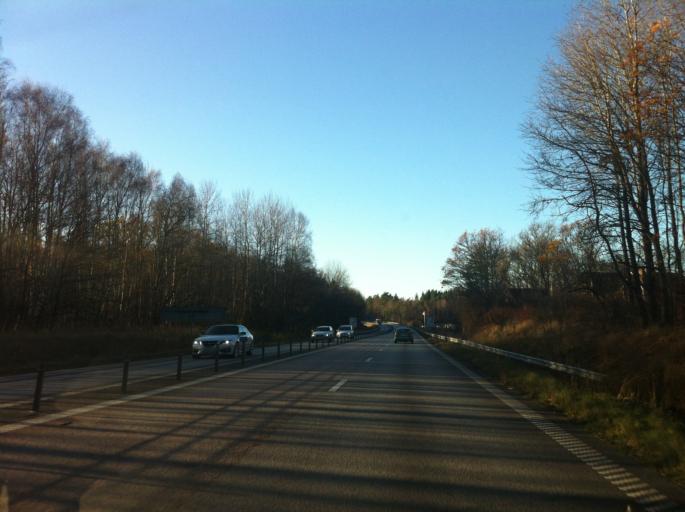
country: SE
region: Blekinge
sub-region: Karlshamns Kommun
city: Karlshamn
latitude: 56.1885
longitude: 14.8073
